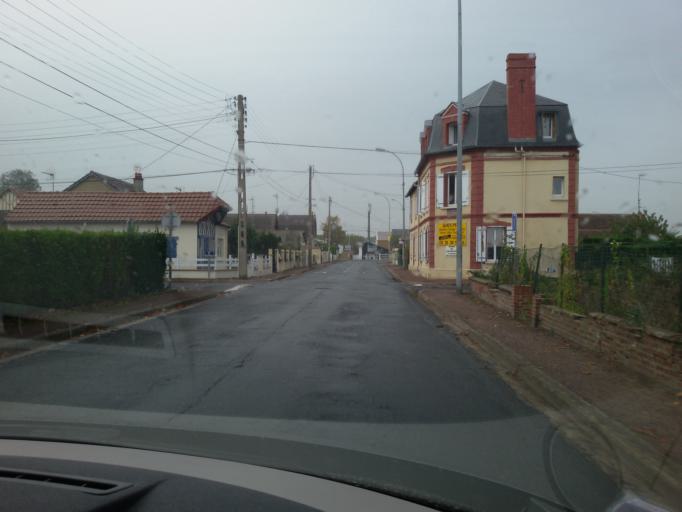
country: FR
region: Lower Normandy
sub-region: Departement du Calvados
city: Houlgate
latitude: 49.2938
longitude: -0.0919
